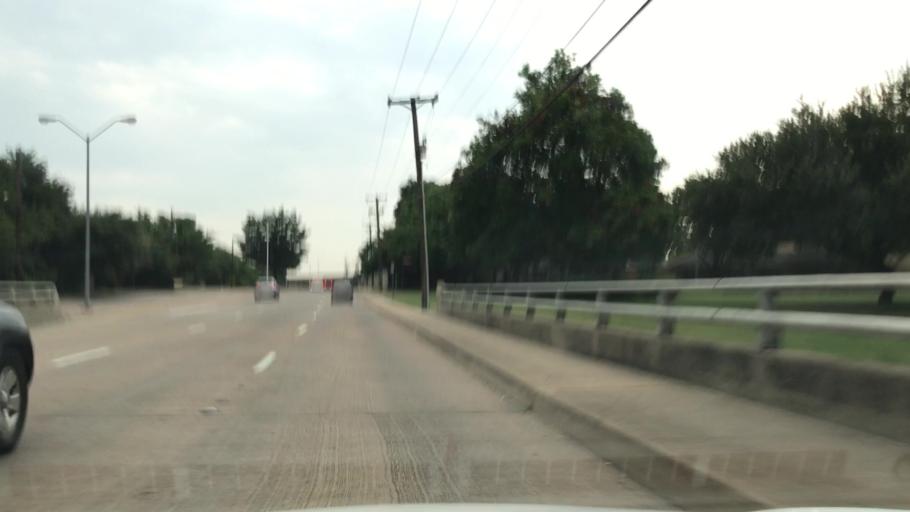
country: US
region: Texas
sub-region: Dallas County
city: Farmers Branch
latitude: 32.9157
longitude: -96.8818
